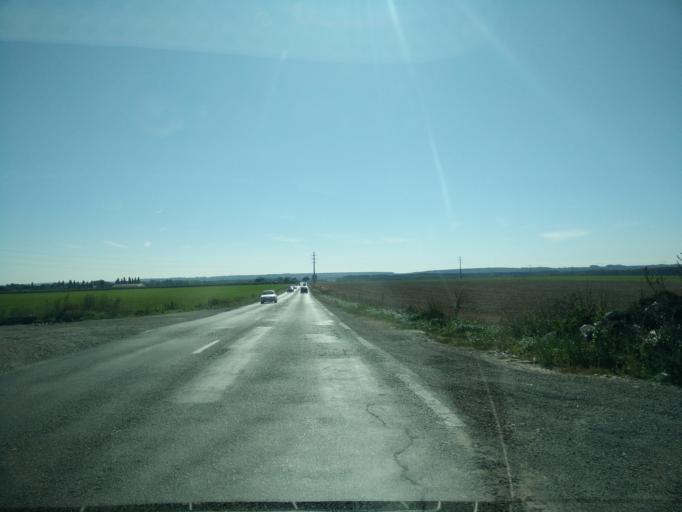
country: FR
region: Ile-de-France
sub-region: Departement de Seine-et-Marne
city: Claye-Souilly
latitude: 48.9772
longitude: 2.6603
